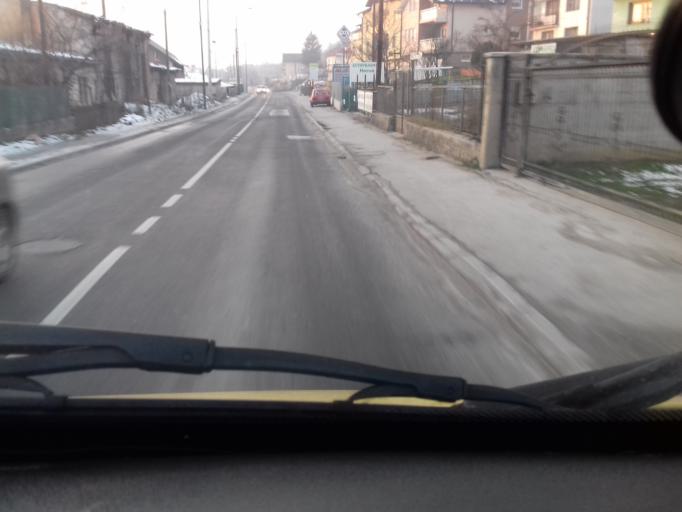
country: BA
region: Federation of Bosnia and Herzegovina
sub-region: Kanton Sarajevo
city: Sarajevo
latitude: 43.8530
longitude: 18.3328
